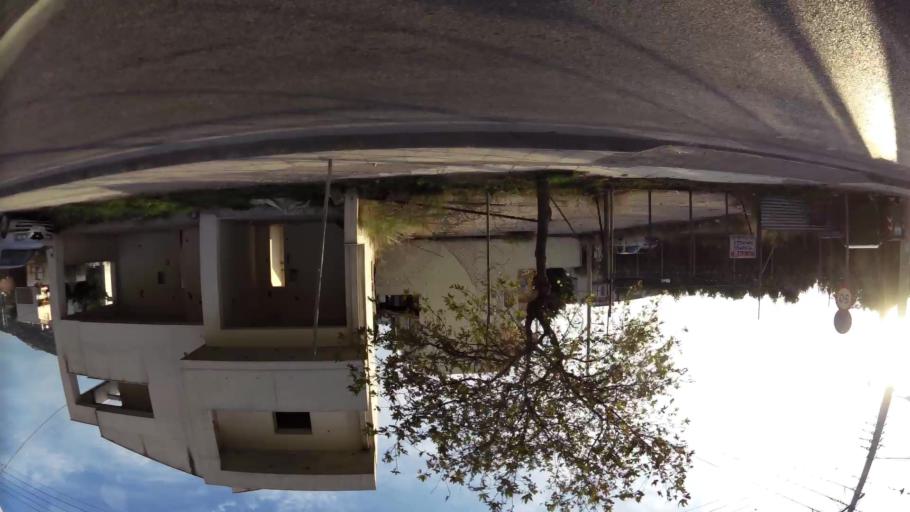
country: GR
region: Attica
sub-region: Nomarchia Dytikis Attikis
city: Ano Liosia
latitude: 38.0710
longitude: 23.6933
